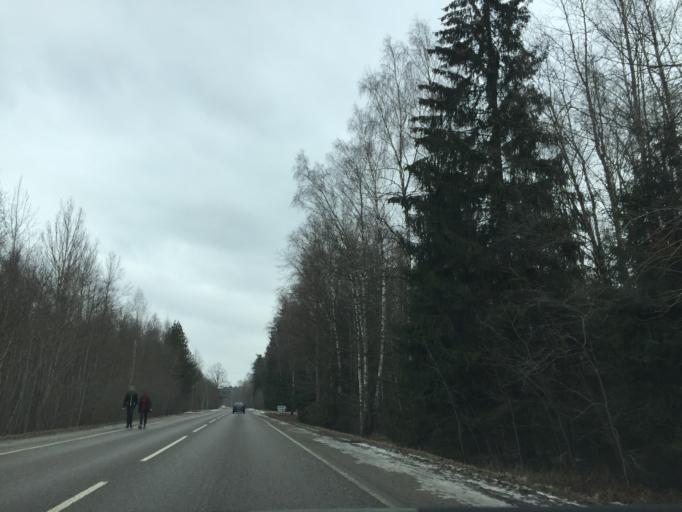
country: LV
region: Kegums
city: Kegums
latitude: 56.7550
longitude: 24.7369
